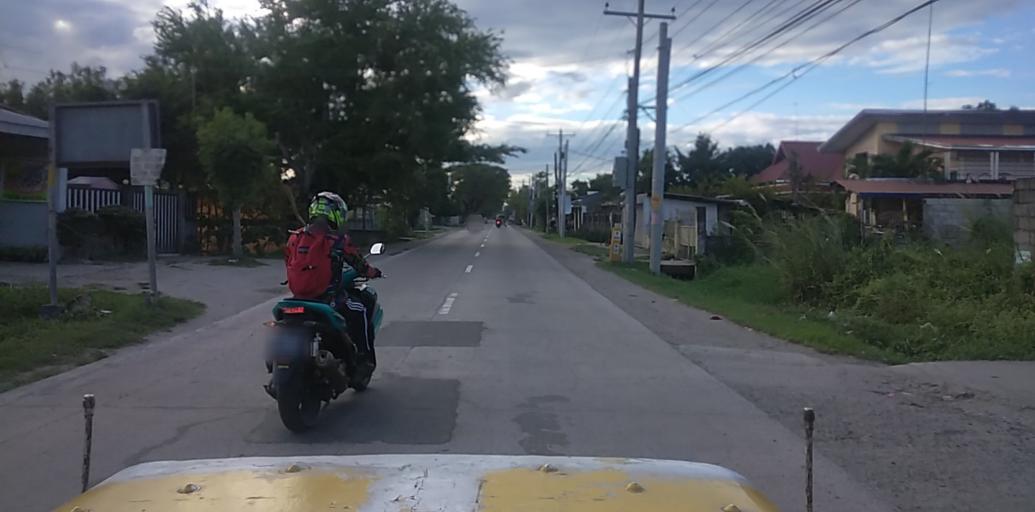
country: PH
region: Central Luzon
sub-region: Province of Pampanga
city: Arayat
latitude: 15.1519
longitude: 120.7404
